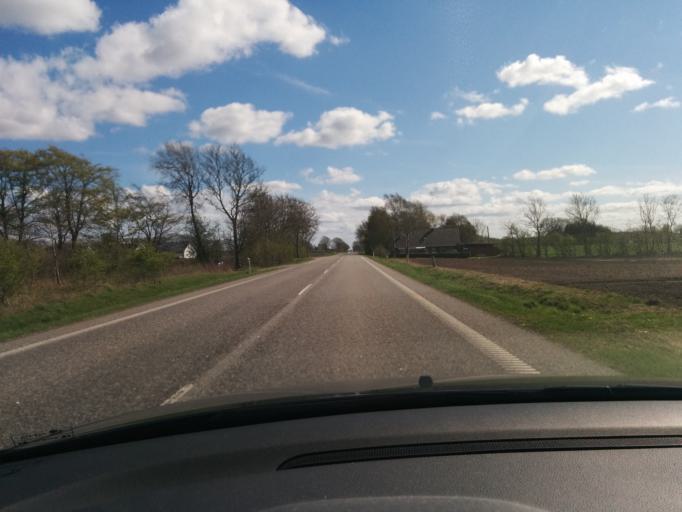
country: DK
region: South Denmark
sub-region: Kolding Kommune
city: Kolding
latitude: 55.4254
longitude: 9.4761
